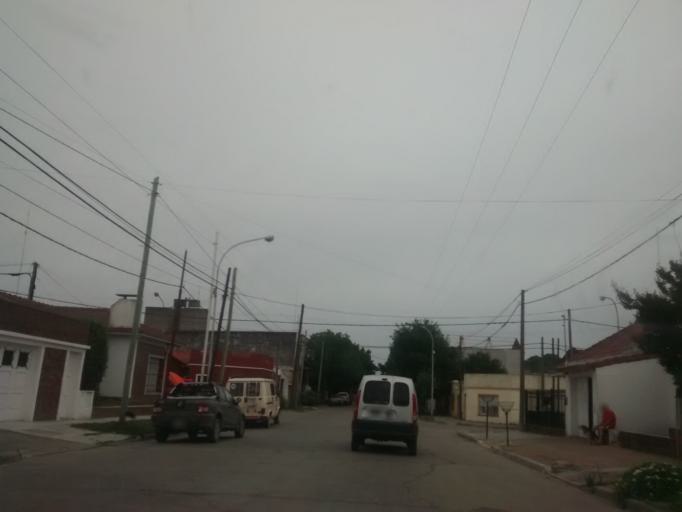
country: AR
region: Buenos Aires
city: Necochea
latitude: -38.5607
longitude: -58.7290
